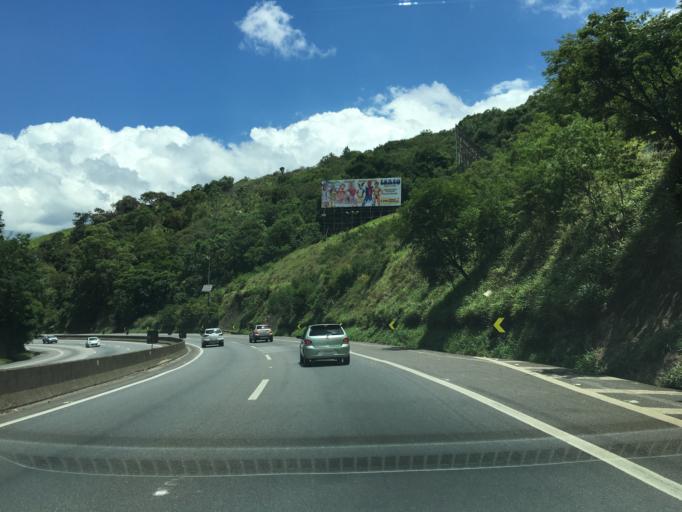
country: BR
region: Sao Paulo
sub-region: Mairipora
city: Mairipora
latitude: -23.2910
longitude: -46.5799
